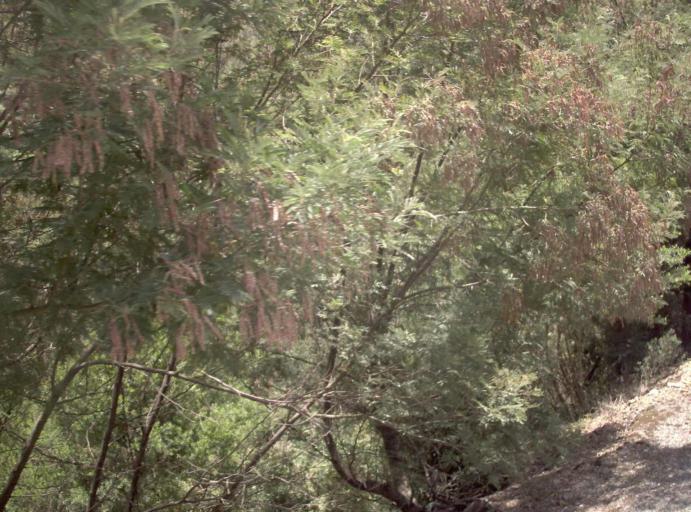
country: AU
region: Victoria
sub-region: East Gippsland
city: Lakes Entrance
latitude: -37.5506
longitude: 147.8728
